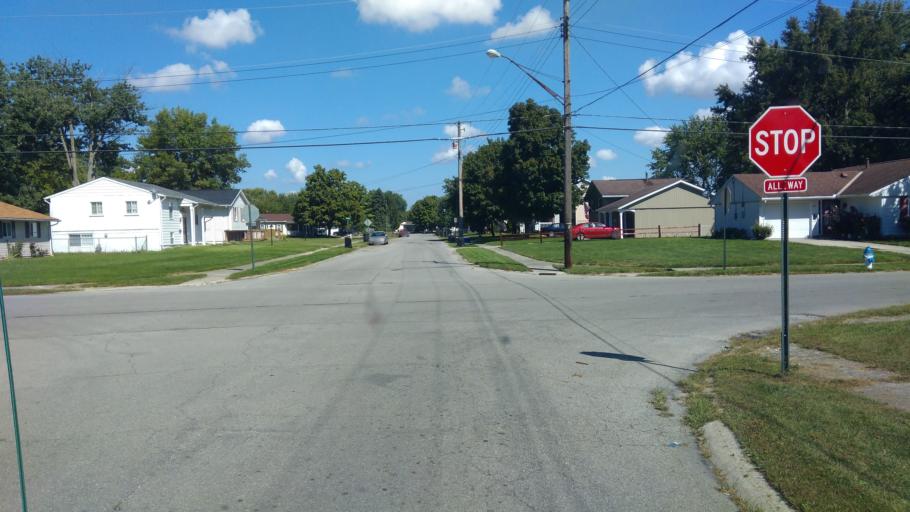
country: US
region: Ohio
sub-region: Marion County
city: Marion
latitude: 40.6107
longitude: -83.1183
